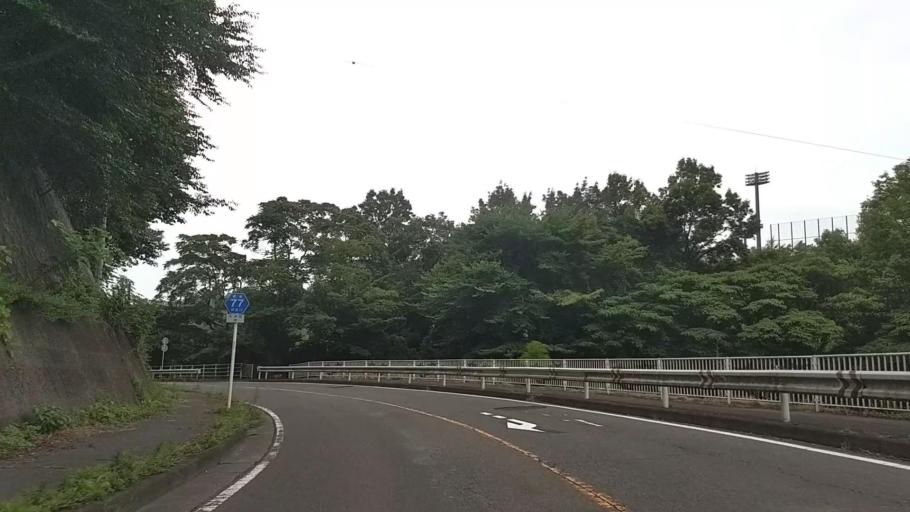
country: JP
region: Kanagawa
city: Hadano
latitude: 35.3405
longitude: 139.2218
